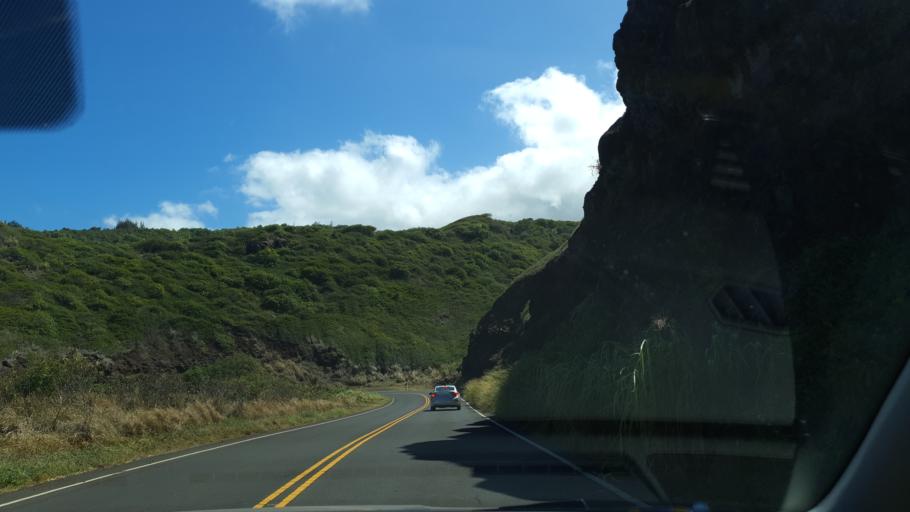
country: US
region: Hawaii
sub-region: Maui County
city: Waihee-Waiehu
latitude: 21.0115
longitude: -156.5693
